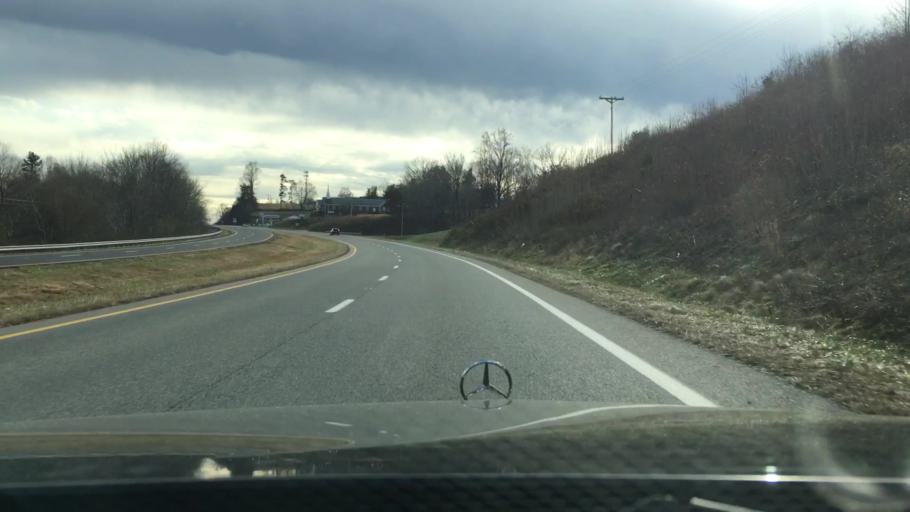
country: US
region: Virginia
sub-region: Pittsylvania County
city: Motley
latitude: 37.0284
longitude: -79.3586
